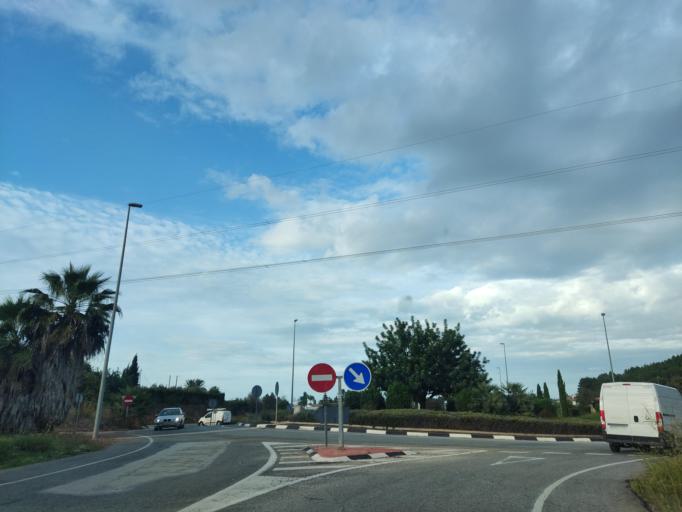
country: ES
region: Valencia
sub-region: Provincia de Alicante
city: Pedreguer
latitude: 38.8067
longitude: 0.0336
